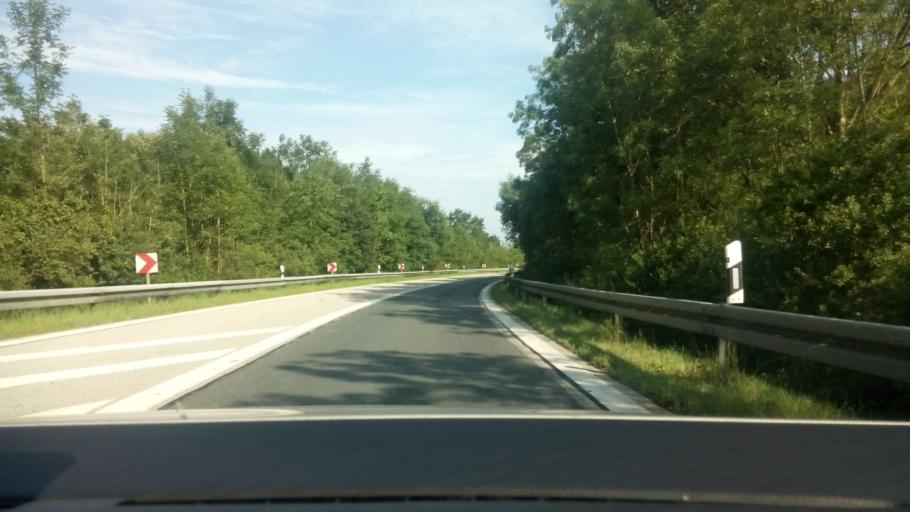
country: DE
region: Bavaria
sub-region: Upper Bavaria
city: Oberschleissheim
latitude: 48.2271
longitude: 11.5458
